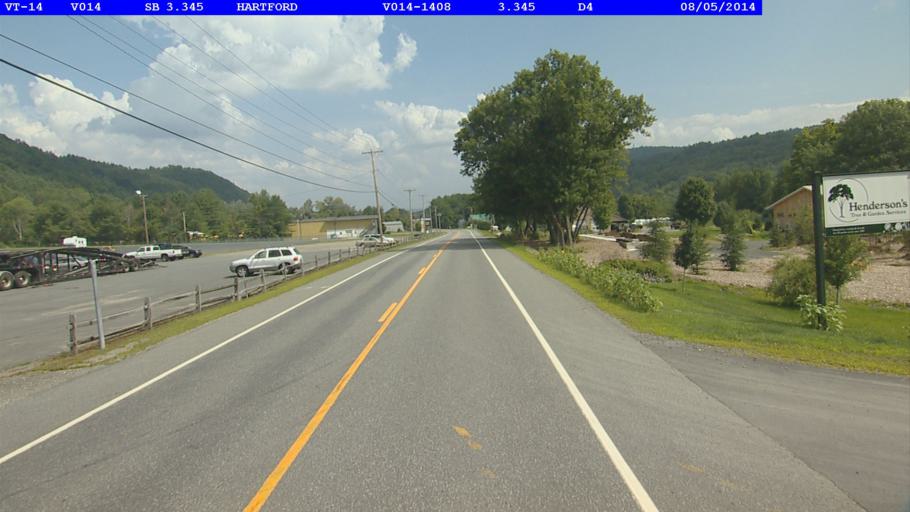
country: US
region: Vermont
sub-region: Windsor County
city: White River Junction
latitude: 43.6721
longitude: -72.3784
